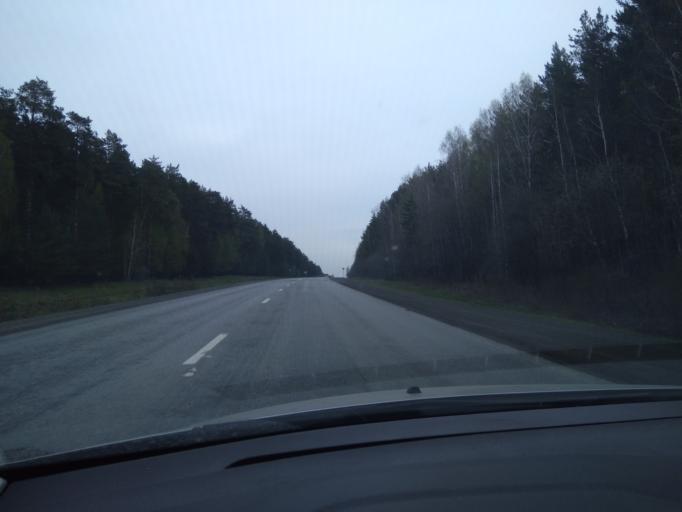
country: RU
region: Sverdlovsk
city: Gryaznovskoye
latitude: 56.7898
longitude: 61.7257
